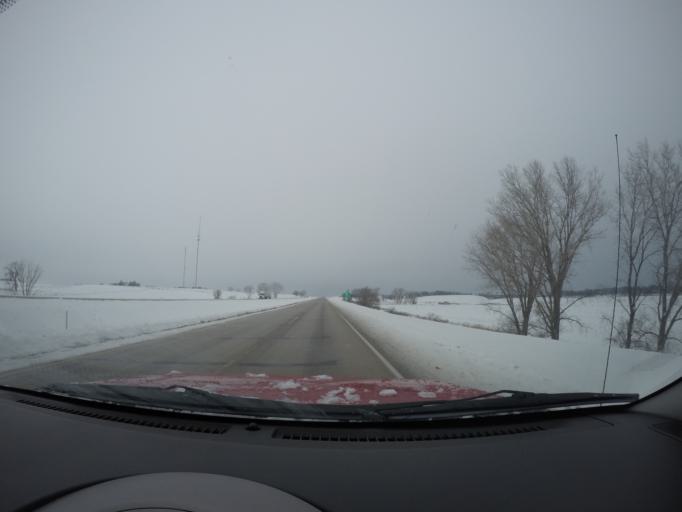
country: US
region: Minnesota
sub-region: Olmsted County
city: Rochester
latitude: 43.9722
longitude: -92.4097
